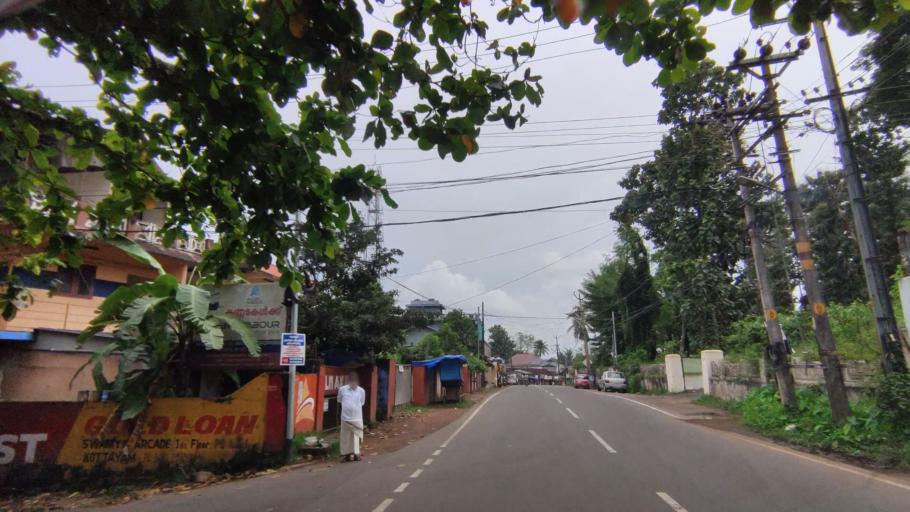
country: IN
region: Kerala
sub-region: Kottayam
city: Kottayam
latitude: 9.5860
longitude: 76.5170
